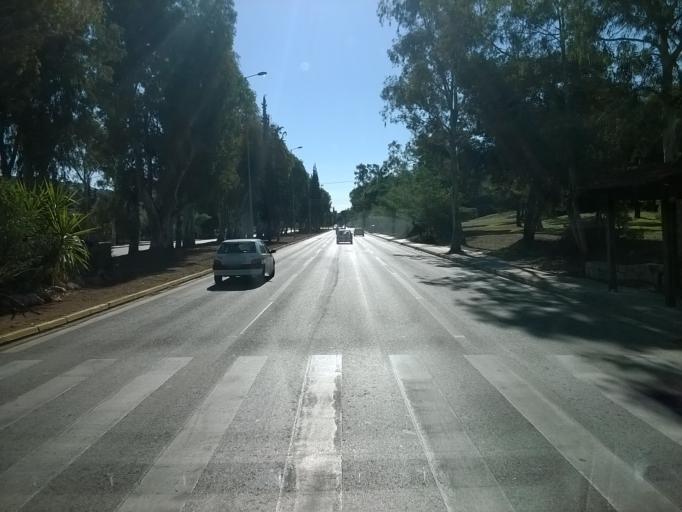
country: GR
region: Attica
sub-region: Nomarchia Anatolikis Attikis
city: Vouliagmeni
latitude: 37.8184
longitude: 23.7770
